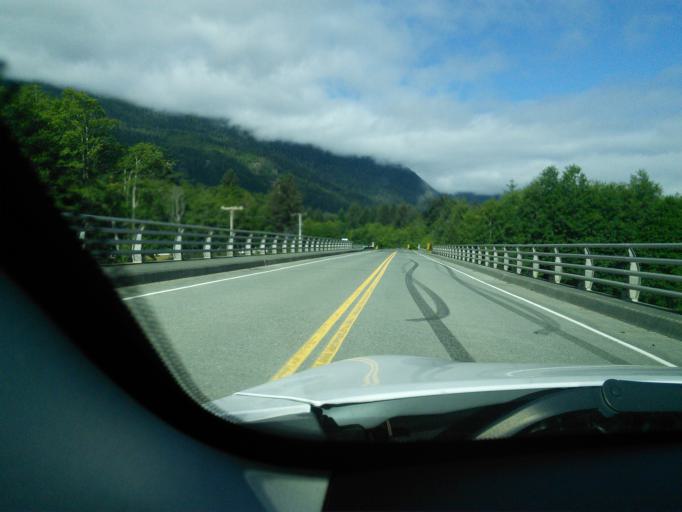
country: CA
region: British Columbia
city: Campbell River
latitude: 50.3612
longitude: -125.9179
